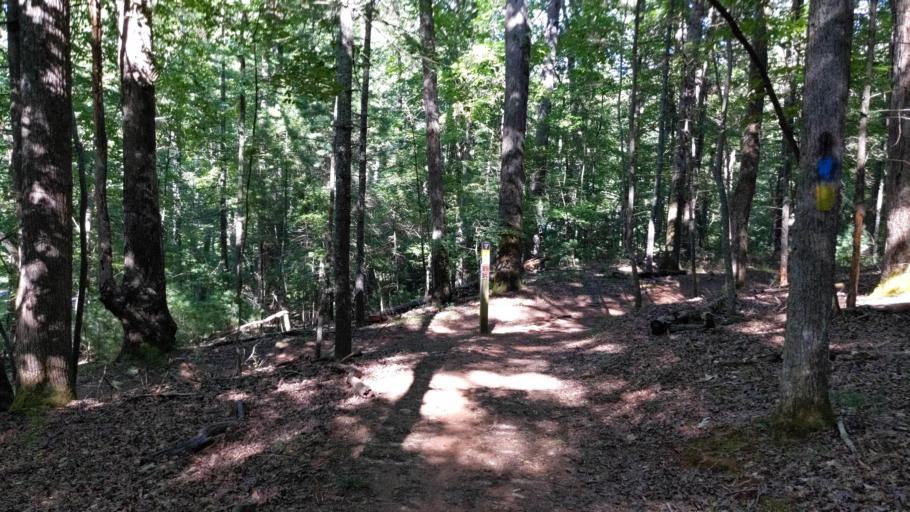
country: US
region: Virginia
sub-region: Henry County
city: Bassett
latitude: 36.7959
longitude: -80.1091
